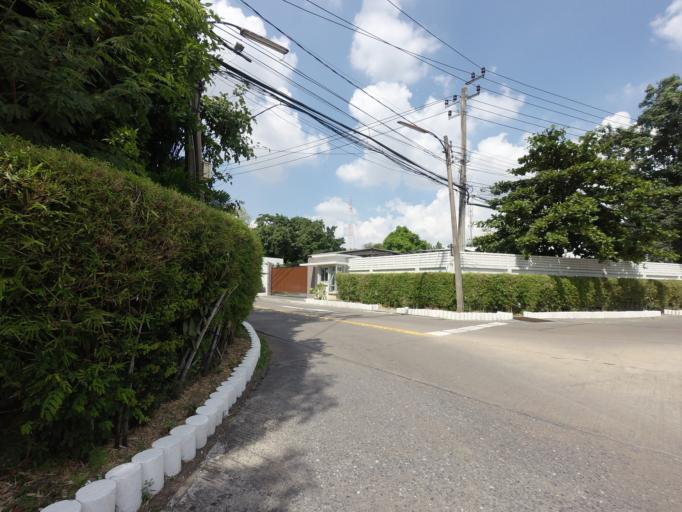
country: TH
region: Bangkok
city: Phaya Thai
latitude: 13.7802
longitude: 100.5523
